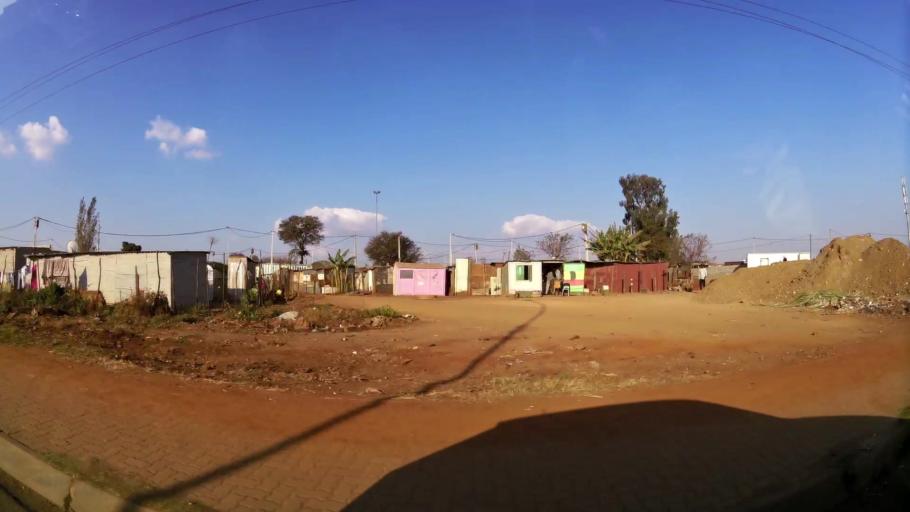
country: ZA
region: Gauteng
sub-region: Ekurhuleni Metropolitan Municipality
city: Tembisa
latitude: -25.9736
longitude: 28.2123
